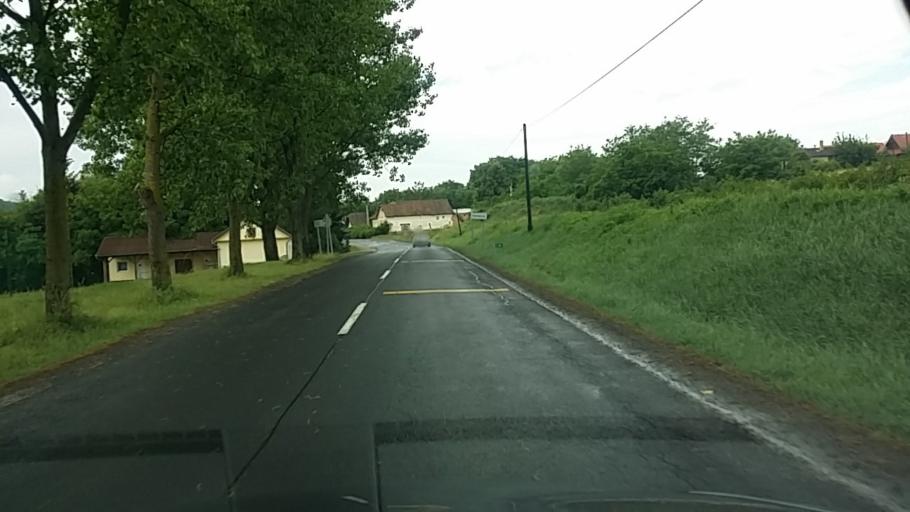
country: SK
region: Nitriansky
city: Sahy
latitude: 48.0273
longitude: 18.8984
